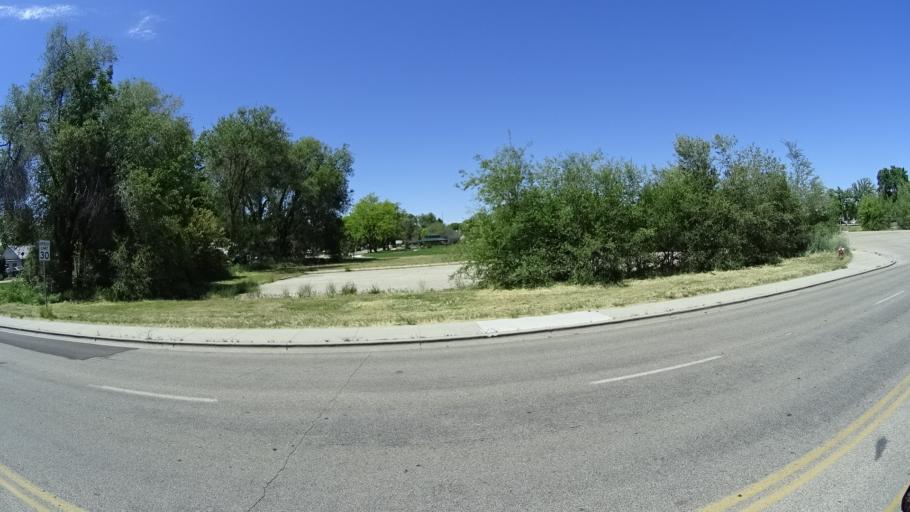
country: US
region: Idaho
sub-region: Ada County
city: Garden City
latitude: 43.6013
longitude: -116.2435
